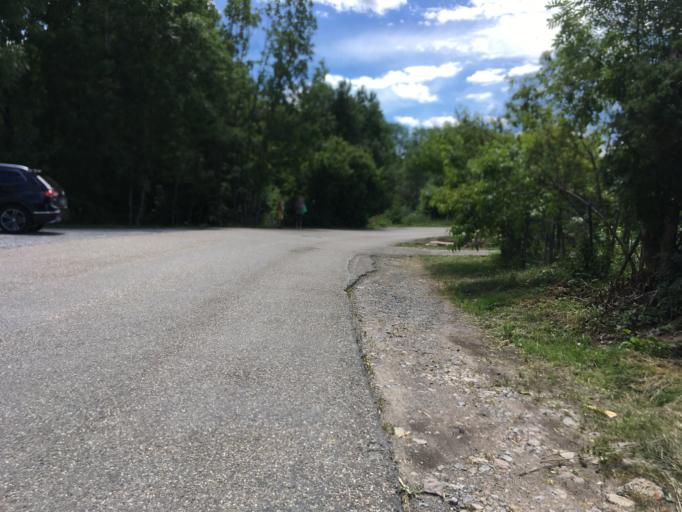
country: DE
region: Baden-Wuerttemberg
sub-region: Regierungsbezirk Stuttgart
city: Vaihingen an der Enz
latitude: 48.9194
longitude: 8.9910
